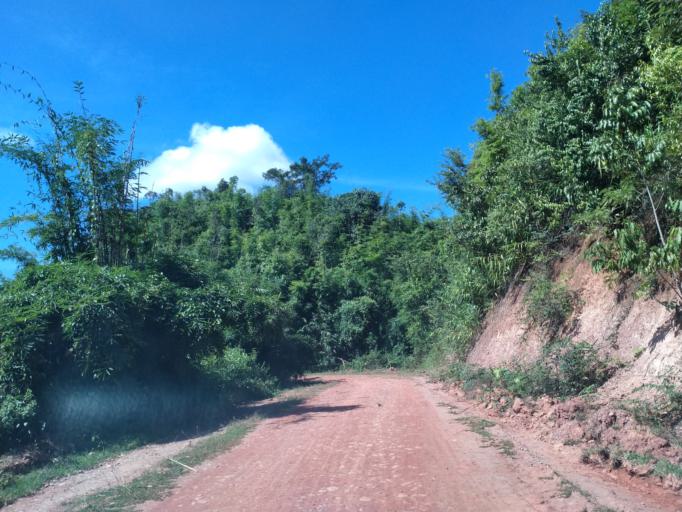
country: LA
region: Vientiane
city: Muang Phon-Hong
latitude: 18.6155
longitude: 102.8535
